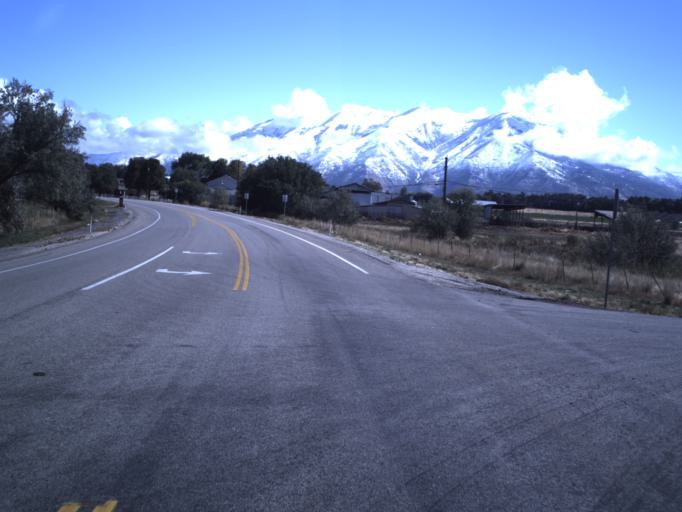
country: US
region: Utah
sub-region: Utah County
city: Salem
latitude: 40.0853
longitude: -111.6723
